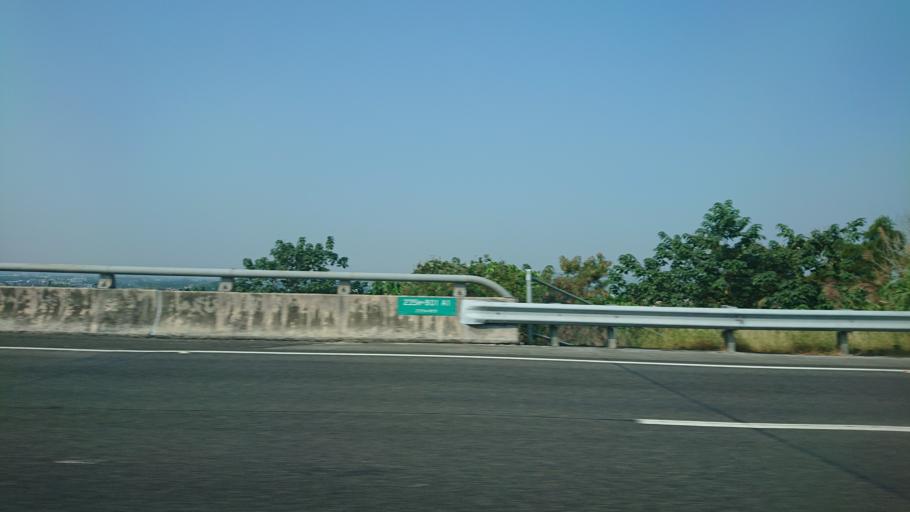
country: TW
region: Taiwan
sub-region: Nantou
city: Nantou
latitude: 23.8636
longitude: 120.7028
